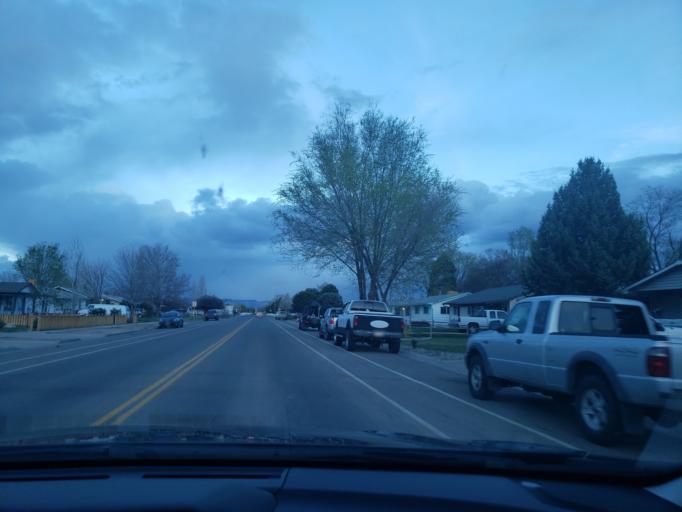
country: US
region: Colorado
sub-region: Mesa County
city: Fruita
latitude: 39.1589
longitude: -108.7218
